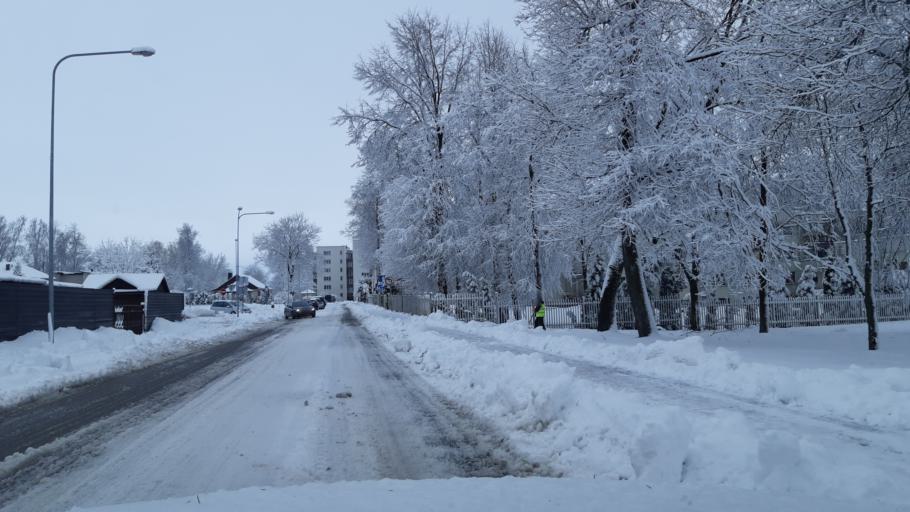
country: LT
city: Kybartai
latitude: 54.6388
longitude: 22.7572
